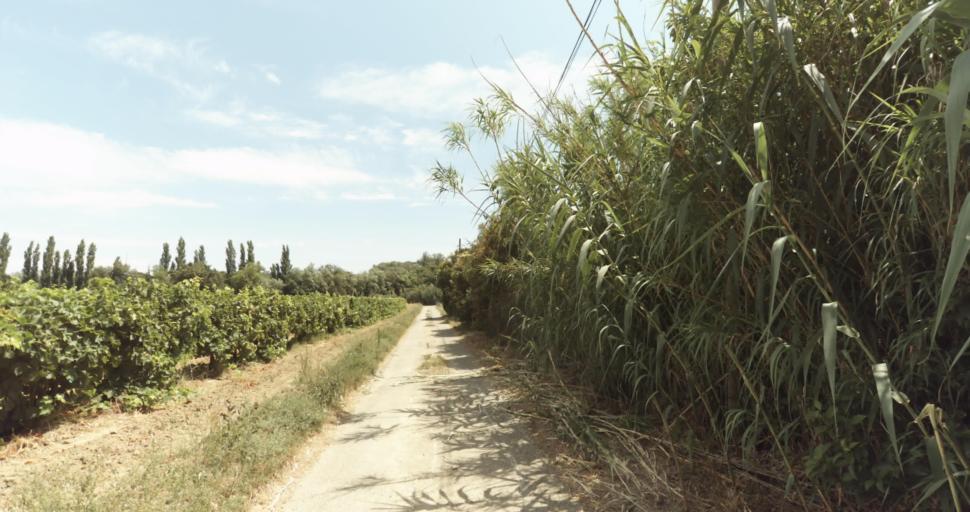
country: FR
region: Provence-Alpes-Cote d'Azur
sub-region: Departement du Vaucluse
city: Monteux
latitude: 44.0512
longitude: 5.0205
